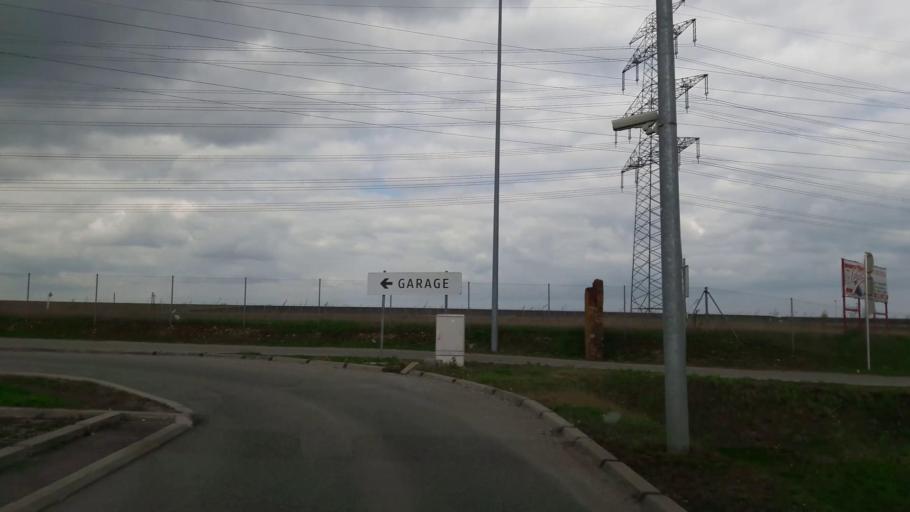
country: AT
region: Lower Austria
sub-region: Politischer Bezirk Mistelbach
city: Grossebersdorf
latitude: 48.3453
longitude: 16.4652
